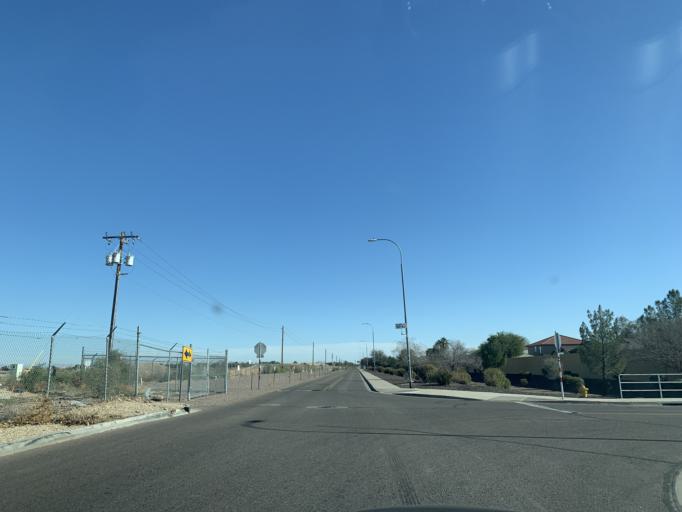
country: US
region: Arizona
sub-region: Maricopa County
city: Laveen
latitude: 33.3994
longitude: -112.1253
